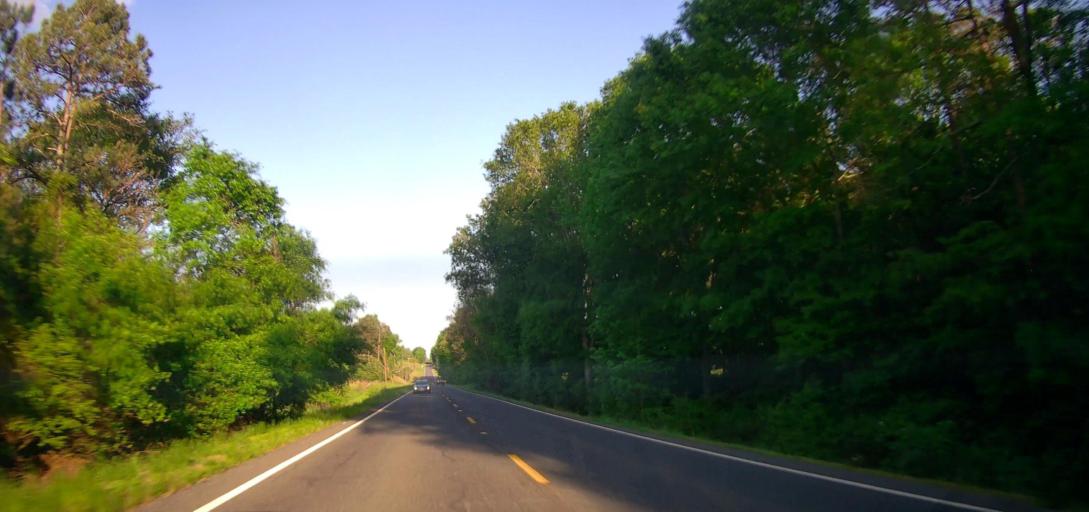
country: US
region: Georgia
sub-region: Walton County
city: Social Circle
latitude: 33.5076
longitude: -83.6668
